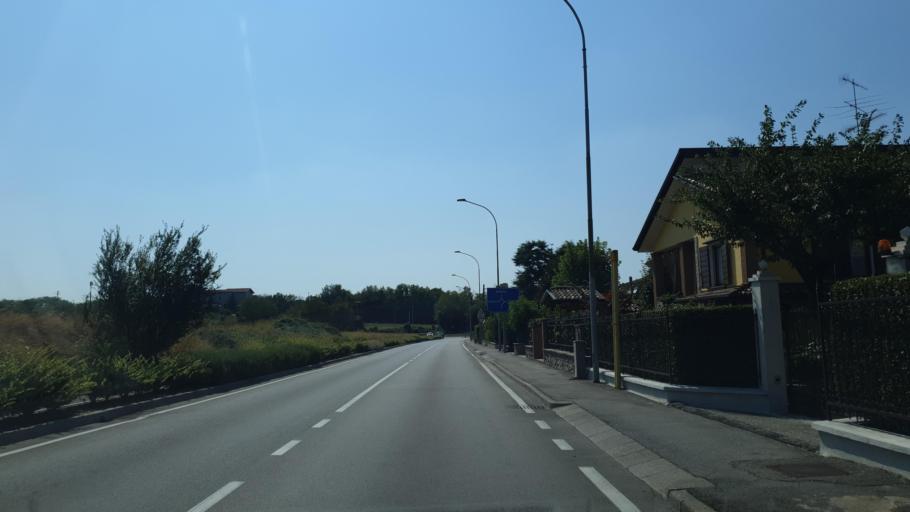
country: IT
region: Lombardy
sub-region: Provincia di Brescia
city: Calvagese della Riviera
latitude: 45.5325
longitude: 10.4439
